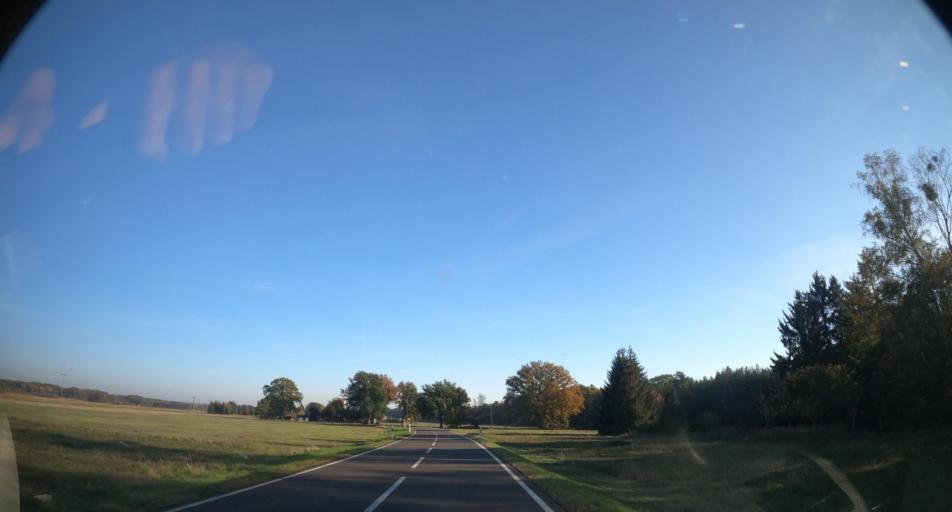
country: DE
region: Mecklenburg-Vorpommern
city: Ahlbeck
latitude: 53.6202
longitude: 14.2422
